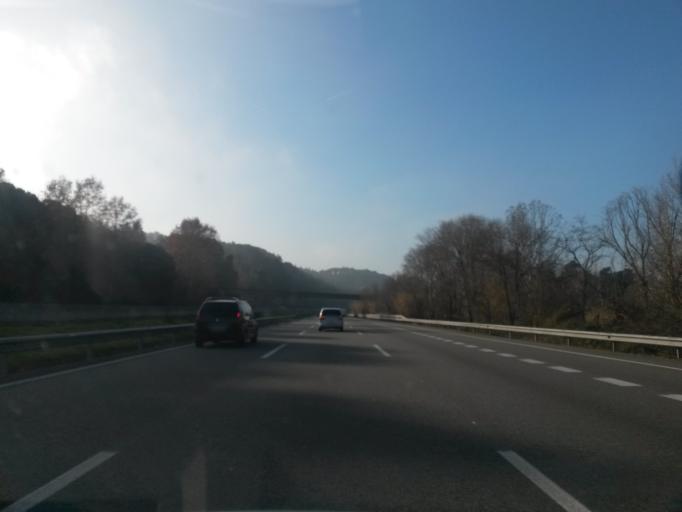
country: ES
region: Catalonia
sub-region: Provincia de Barcelona
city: Sant Celoni
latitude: 41.6978
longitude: 2.5145
